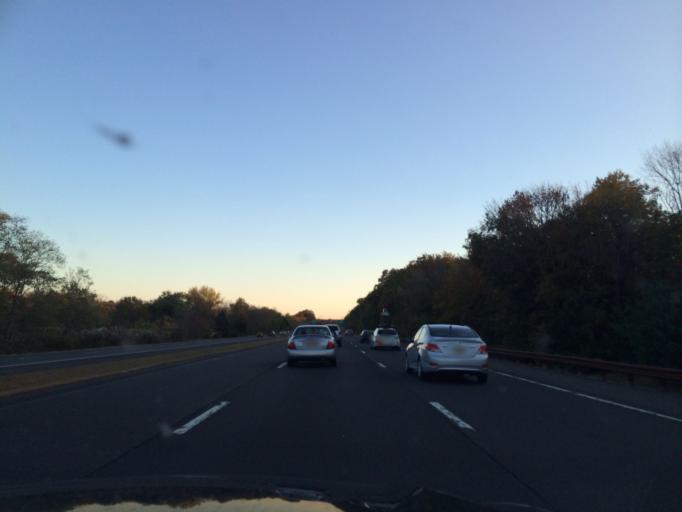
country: US
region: New Jersey
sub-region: Monmouth County
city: Tinton Falls
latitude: 40.3049
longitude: -74.0943
